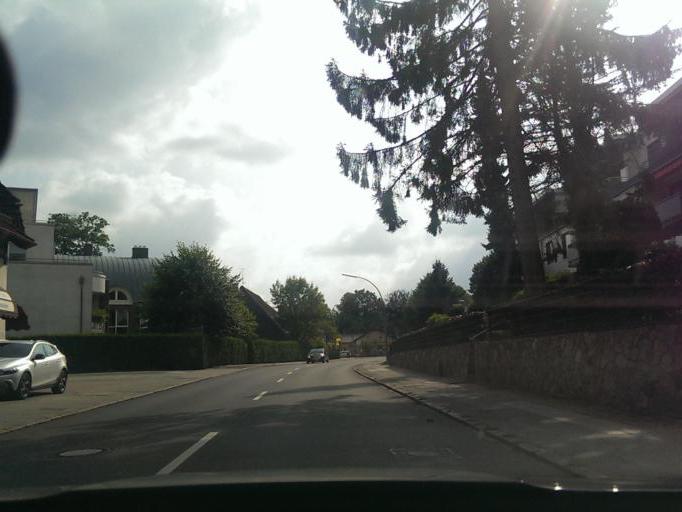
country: DE
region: Hamburg
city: Poppenbuettel
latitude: 53.6635
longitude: 10.0887
